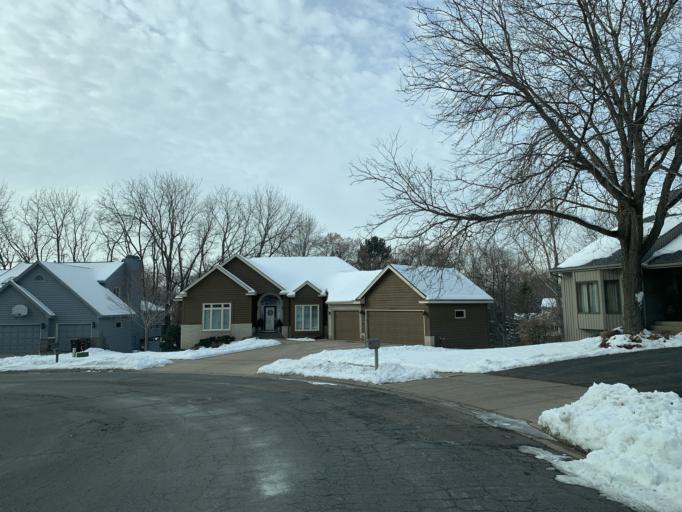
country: US
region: Minnesota
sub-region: Scott County
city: Savage
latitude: 44.8300
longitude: -93.3520
